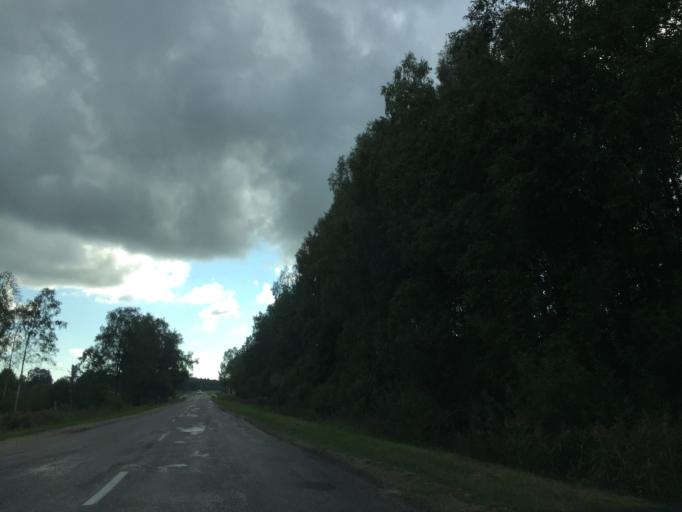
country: LV
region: Limbazu Rajons
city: Limbazi
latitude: 57.3710
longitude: 24.6819
